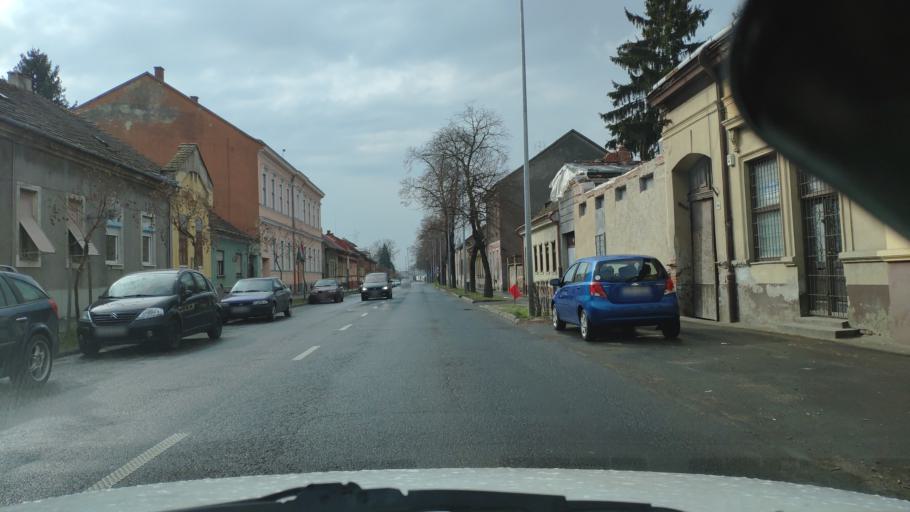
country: HU
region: Zala
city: Nagykanizsa
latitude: 46.4466
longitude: 16.9907
